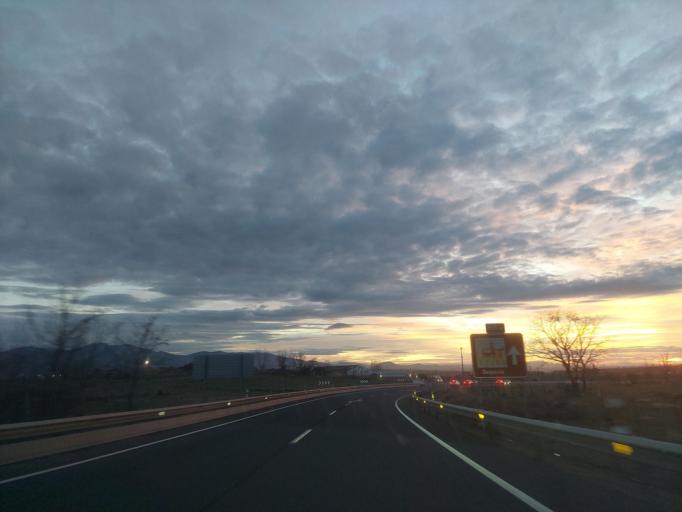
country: ES
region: Castille and Leon
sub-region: Provincia de Segovia
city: San Cristobal de Segovia
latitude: 40.9748
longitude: -4.0785
